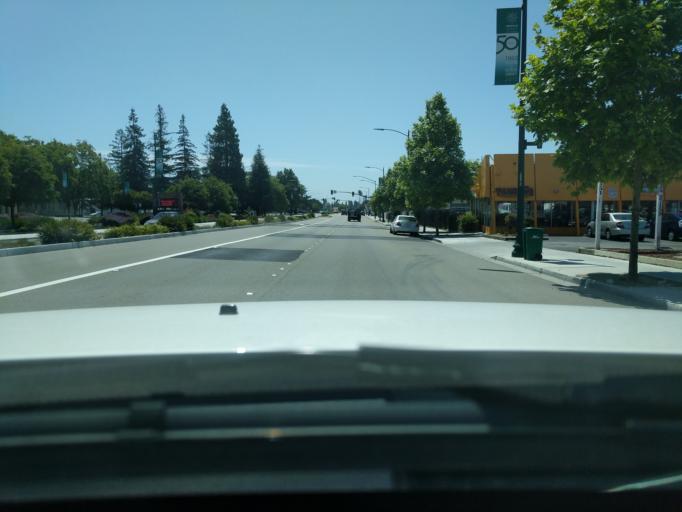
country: US
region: California
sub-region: Alameda County
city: Hayward
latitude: 37.6438
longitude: -122.0613
